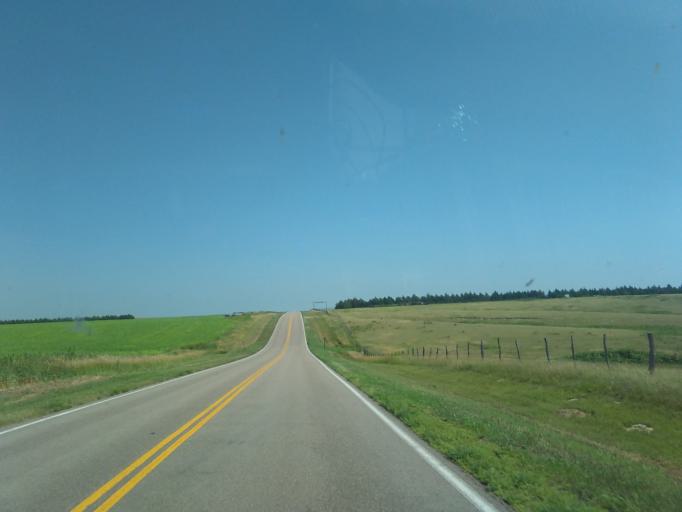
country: US
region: Nebraska
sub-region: Dundy County
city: Benkelman
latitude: 39.9053
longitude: -101.5411
